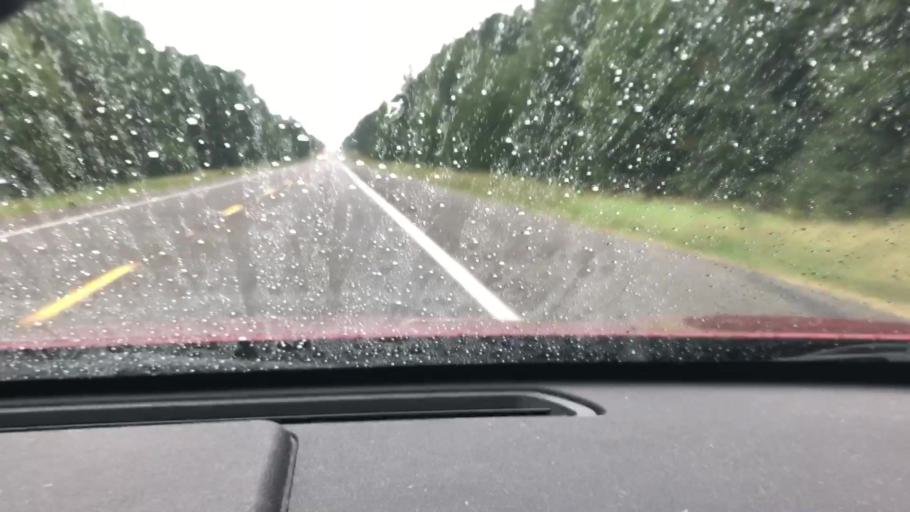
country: US
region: Arkansas
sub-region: Columbia County
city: Magnolia
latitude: 33.3049
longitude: -93.2726
